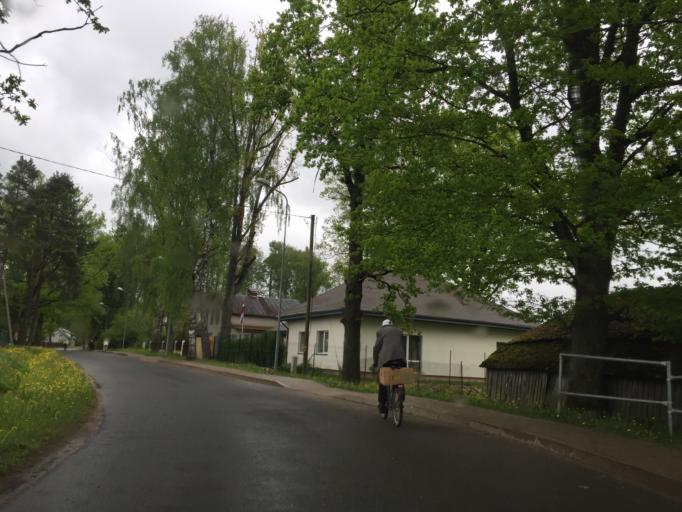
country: LV
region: Lielvarde
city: Lielvarde
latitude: 56.7251
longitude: 24.8048
